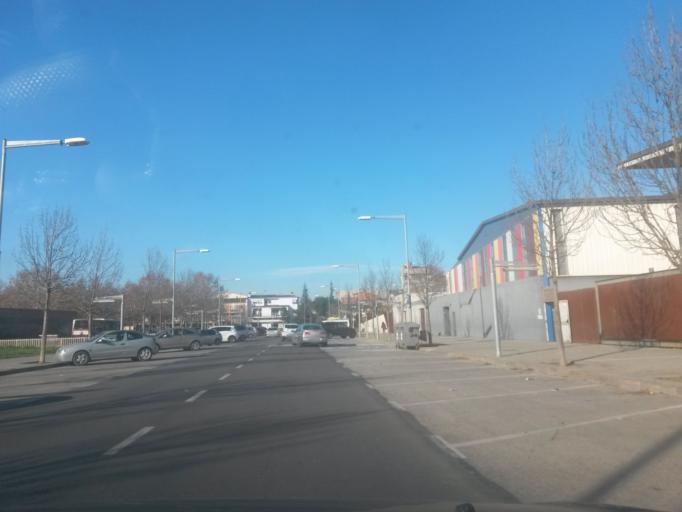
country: ES
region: Catalonia
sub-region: Provincia de Girona
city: Salt
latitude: 41.9696
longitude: 2.7824
